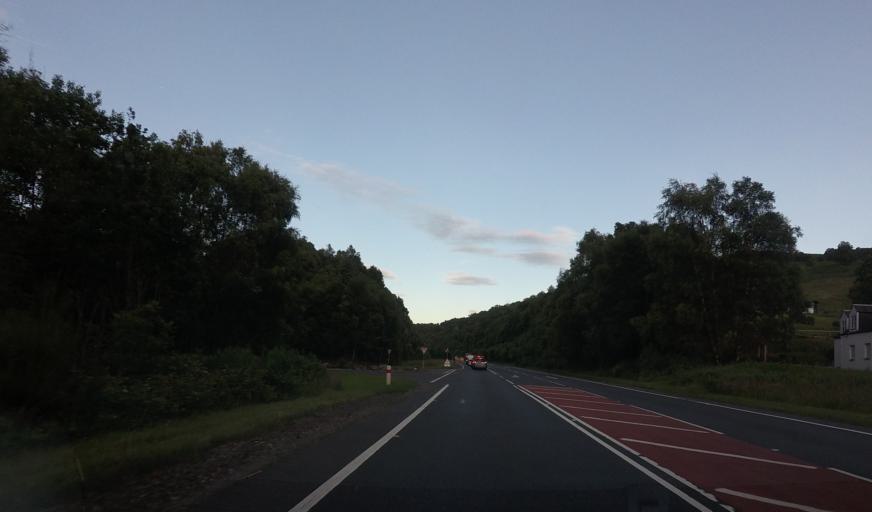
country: GB
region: Scotland
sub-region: Argyll and Bute
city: Helensburgh
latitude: 56.1699
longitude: -4.6782
